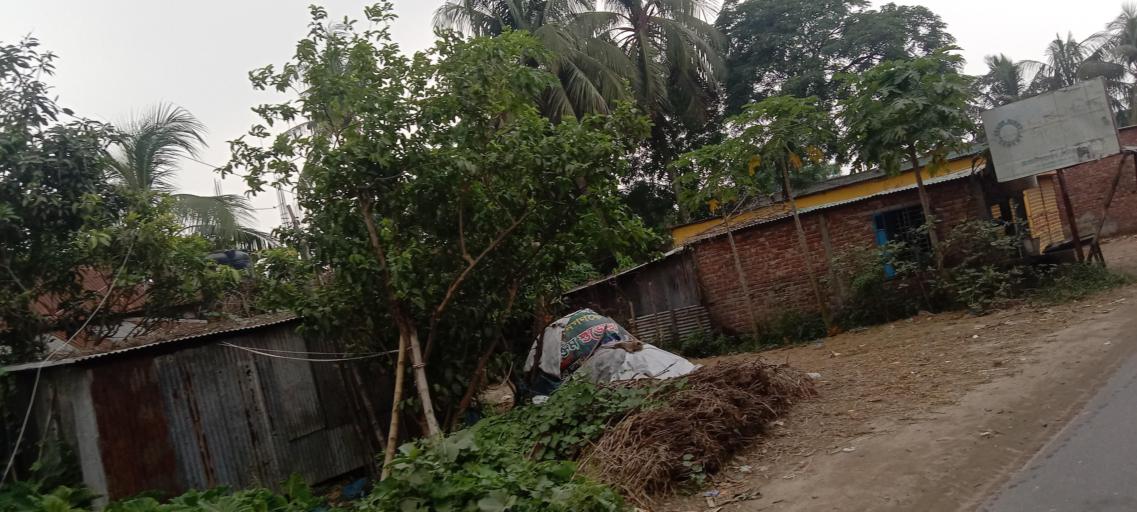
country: BD
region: Dhaka
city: Azimpur
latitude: 23.7400
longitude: 90.3131
